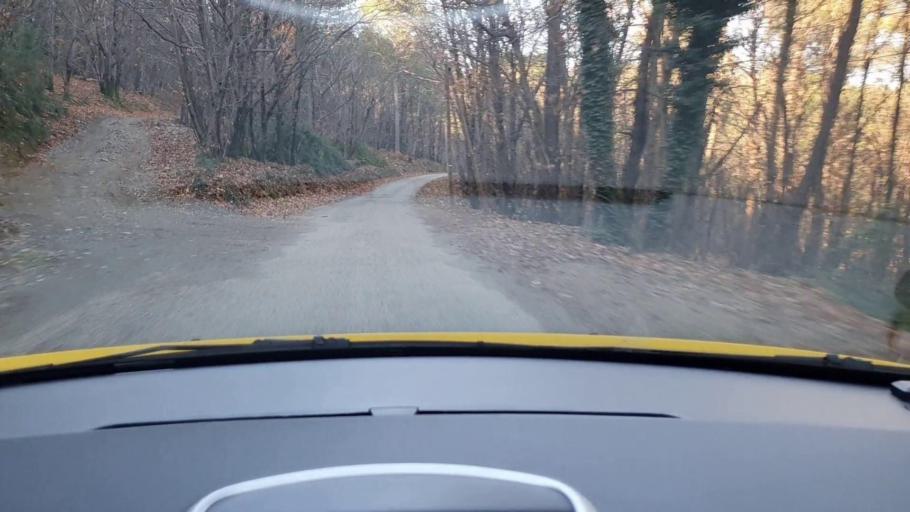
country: FR
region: Languedoc-Roussillon
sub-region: Departement du Gard
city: Branoux-les-Taillades
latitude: 44.2290
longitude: 3.9604
